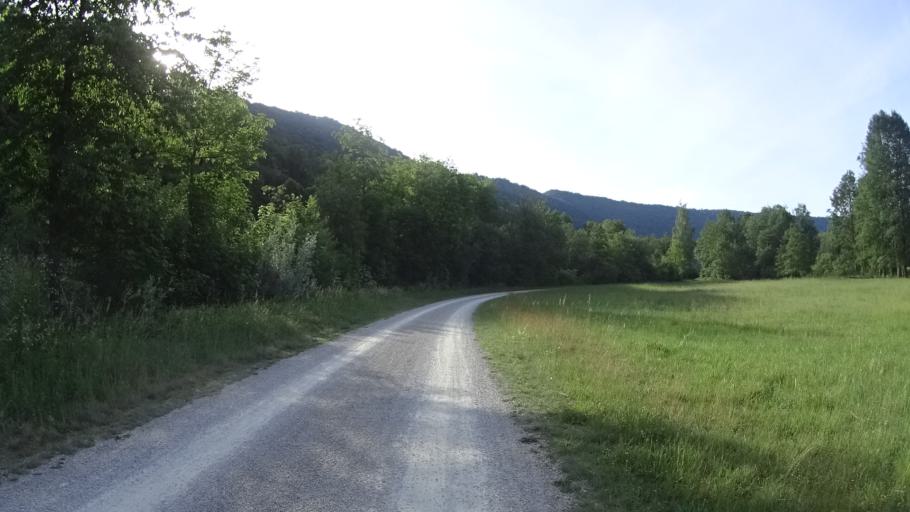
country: DE
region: Bavaria
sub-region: Lower Bavaria
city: Riedenburg
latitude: 48.9923
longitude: 11.6867
